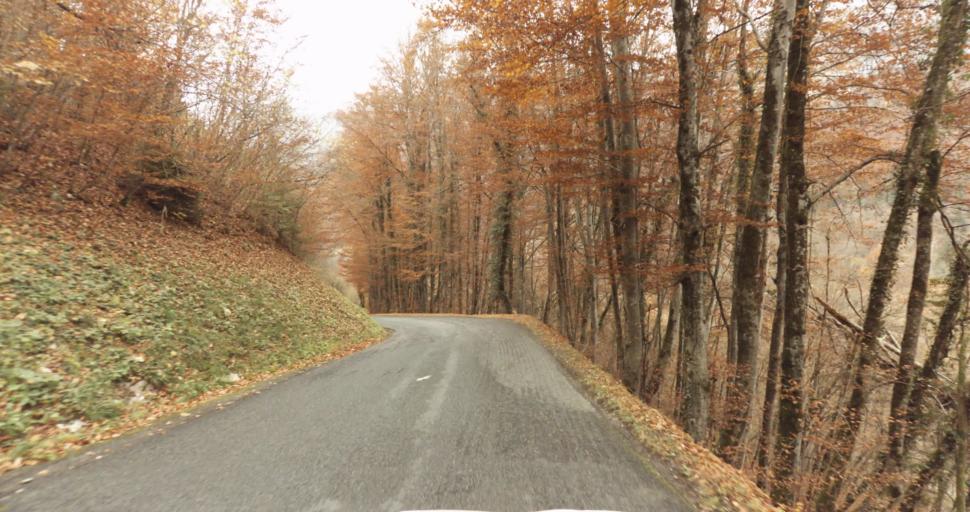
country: FR
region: Rhone-Alpes
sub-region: Departement de la Haute-Savoie
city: Gruffy
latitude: 45.7388
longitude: 6.0952
